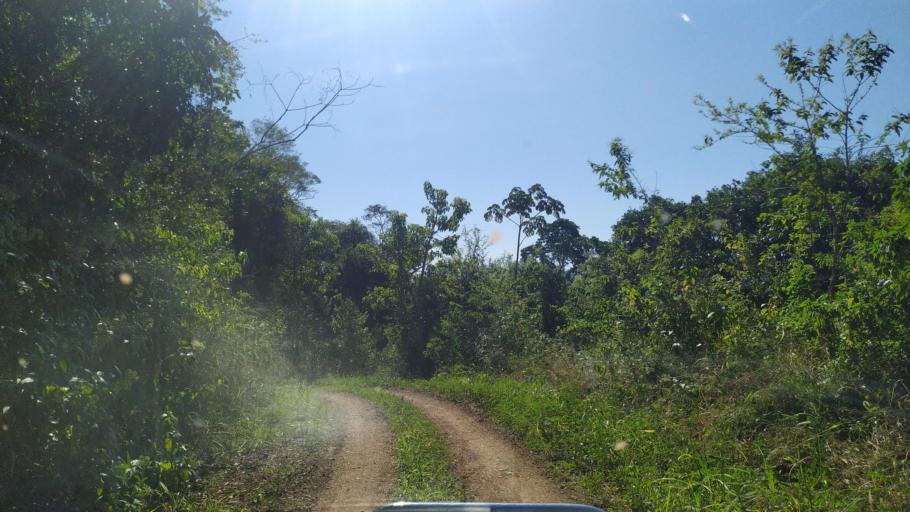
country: AR
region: Misiones
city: El Alcazar
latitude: -26.7626
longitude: -54.5775
